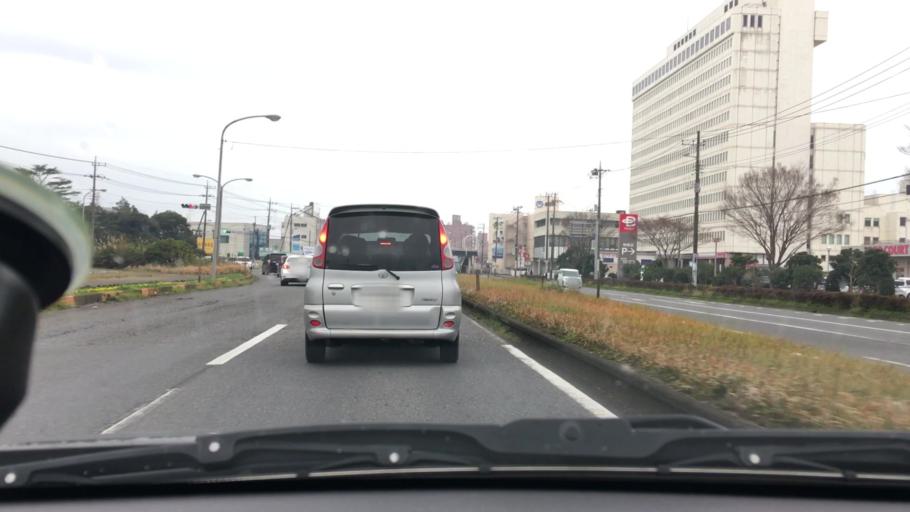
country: JP
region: Chiba
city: Omigawa
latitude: 35.9010
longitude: 140.6365
